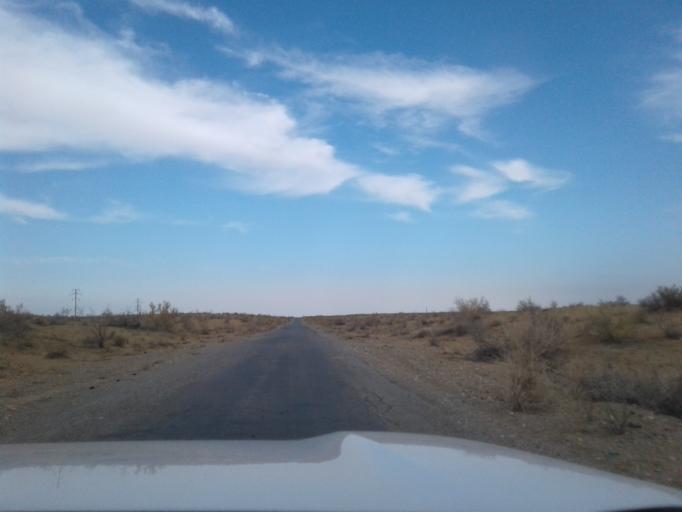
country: TM
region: Lebap
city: Gazojak
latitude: 40.4007
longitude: 61.1898
